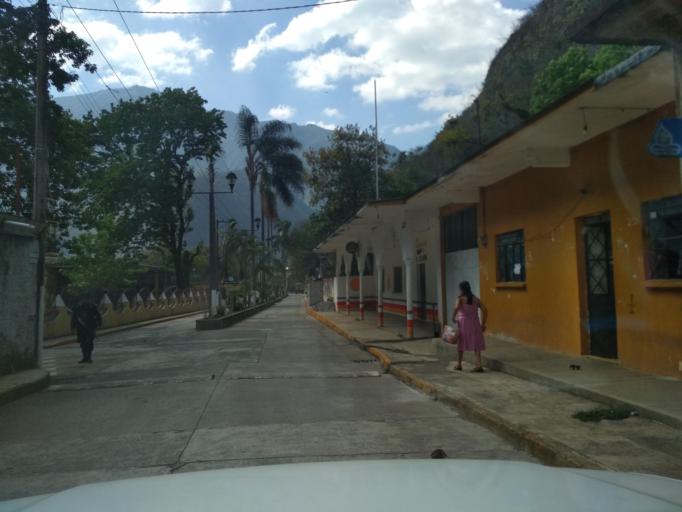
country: MX
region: Veracruz
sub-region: Tlilapan
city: Tonalixco
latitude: 18.7898
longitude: -97.0934
